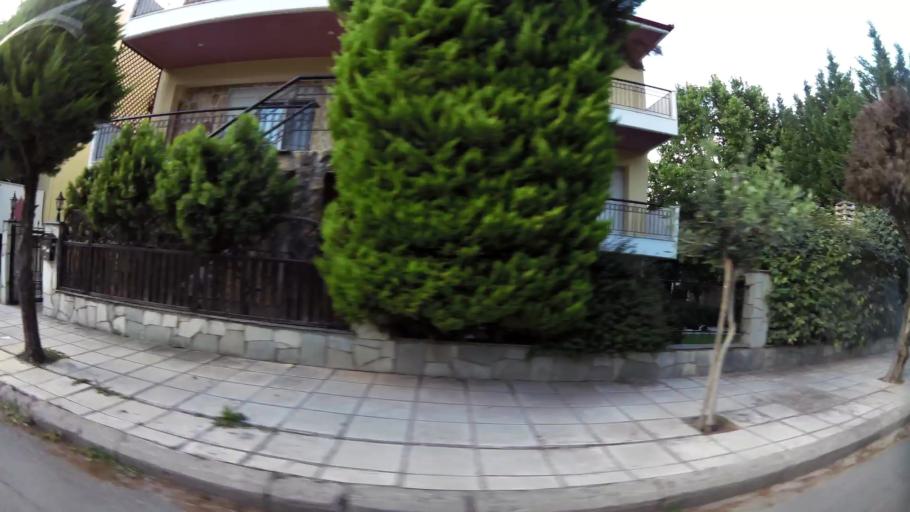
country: GR
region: Central Macedonia
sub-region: Nomos Thessalonikis
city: Pefka
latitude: 40.6566
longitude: 22.9856
